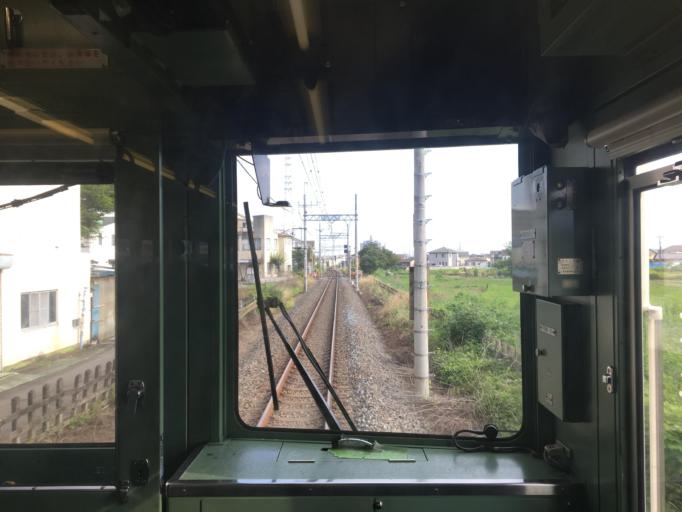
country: JP
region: Tochigi
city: Ashikaga
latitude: 36.3141
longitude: 139.4554
